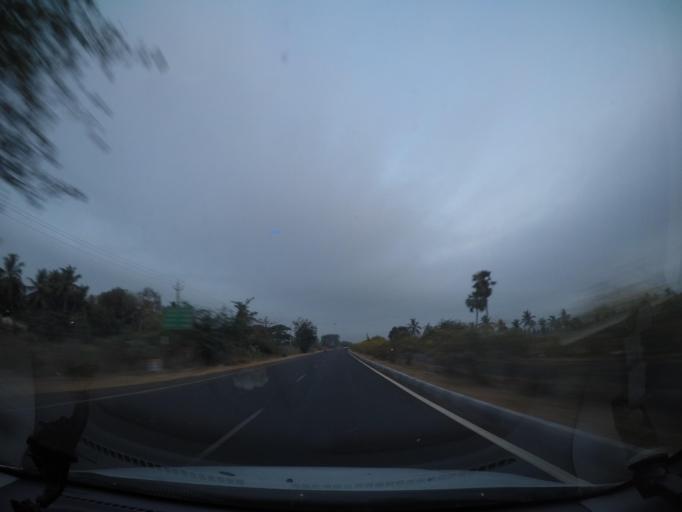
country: IN
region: Andhra Pradesh
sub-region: West Godavari
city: Tadepallegudem
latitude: 16.8100
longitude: 81.3621
